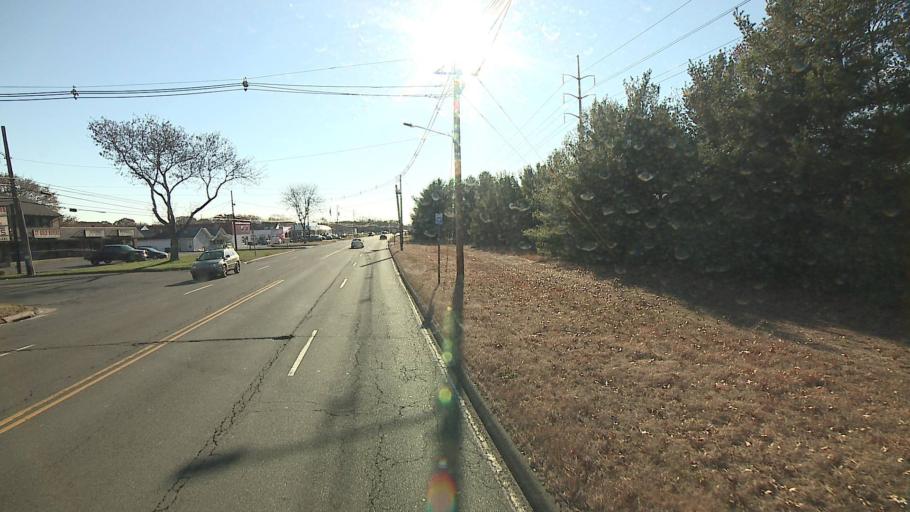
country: US
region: Connecticut
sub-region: New Haven County
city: Wallingford Center
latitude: 41.4336
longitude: -72.8348
